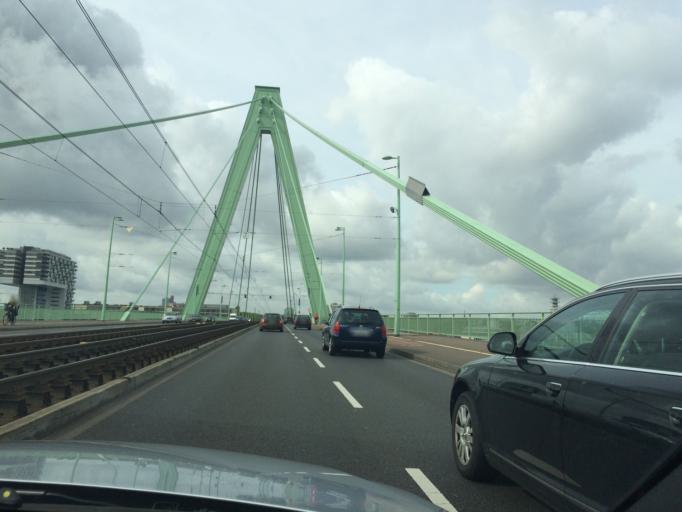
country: DE
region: North Rhine-Westphalia
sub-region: Regierungsbezirk Koln
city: Deutz
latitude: 50.9313
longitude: 6.9717
